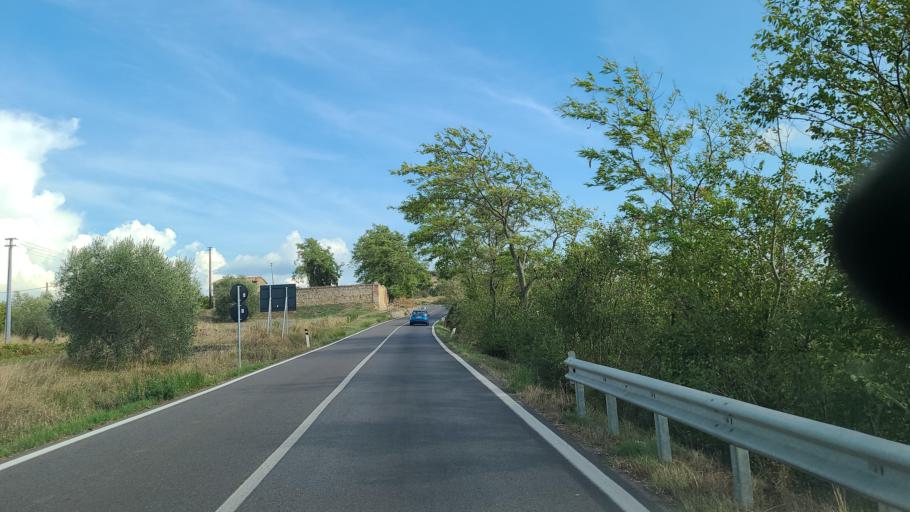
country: IT
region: Tuscany
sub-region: Province of Pisa
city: Volterra
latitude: 43.3915
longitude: 10.8976
